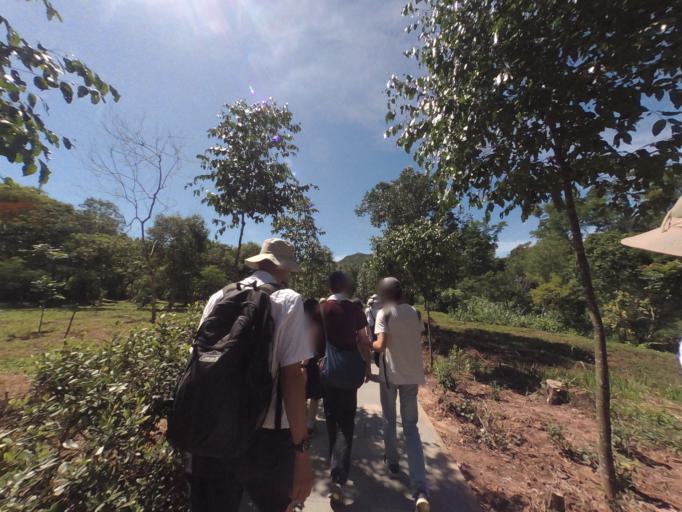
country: VN
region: Quang Nam
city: Dai Loc
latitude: 15.7659
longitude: 108.1231
